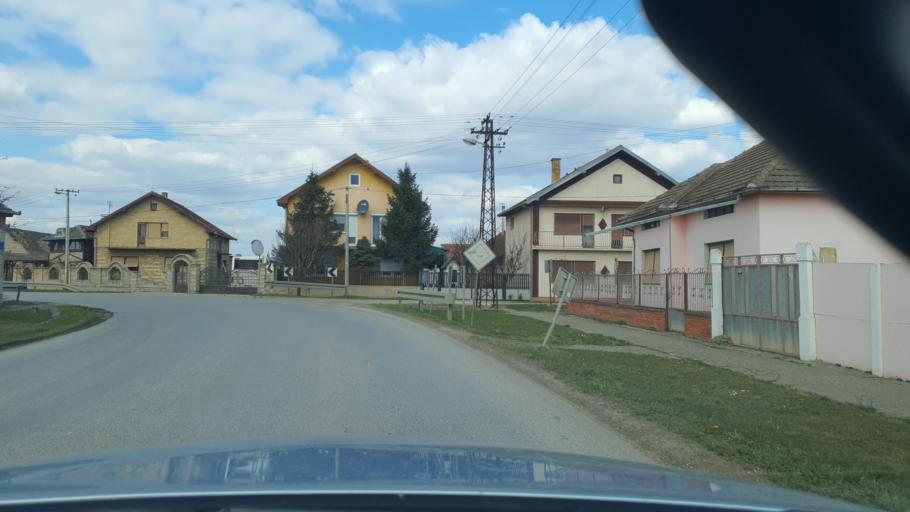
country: RS
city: Maglic
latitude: 45.3970
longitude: 19.4552
